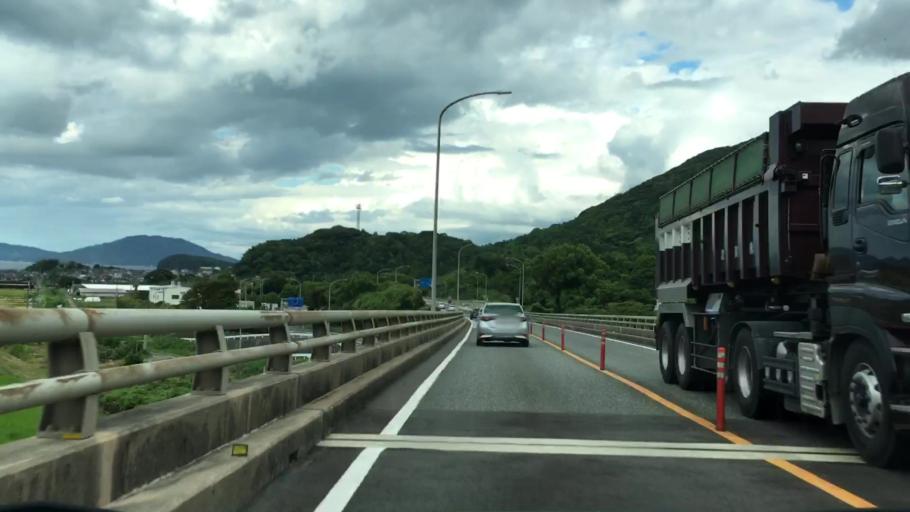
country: JP
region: Saga Prefecture
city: Karatsu
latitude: 33.4936
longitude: 130.0751
